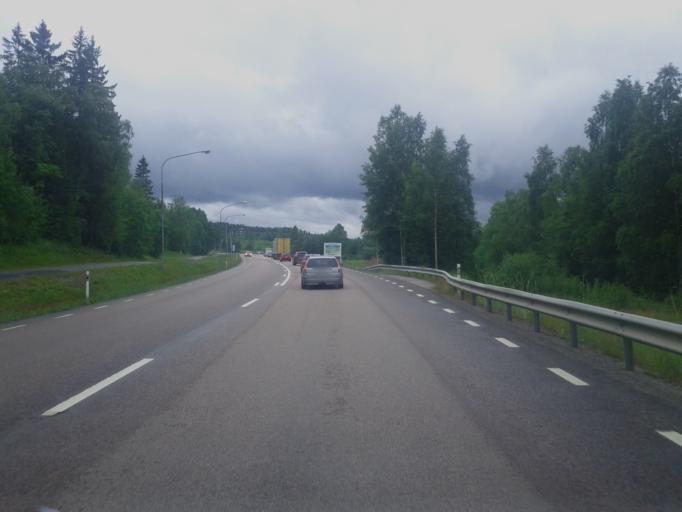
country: SE
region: Vaesternorrland
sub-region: Haernoesands Kommun
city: Haernoesand
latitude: 62.6650
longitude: 17.8500
